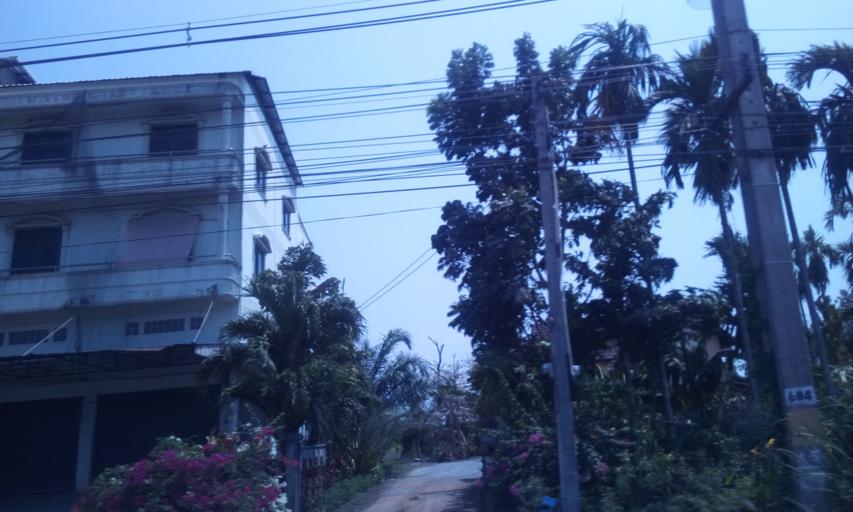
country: TH
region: Chachoengsao
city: Bang Nam Priao
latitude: 13.8245
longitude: 101.0542
